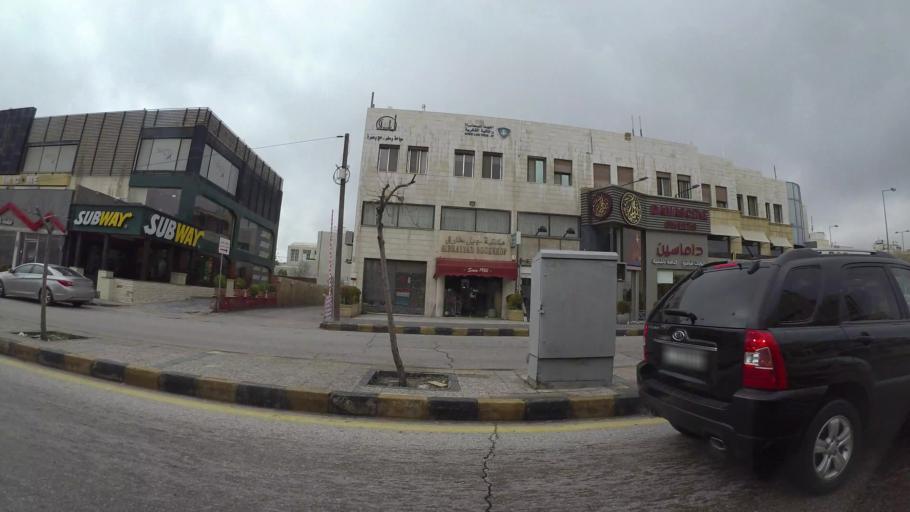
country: JO
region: Amman
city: Amman
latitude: 31.9481
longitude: 35.8923
